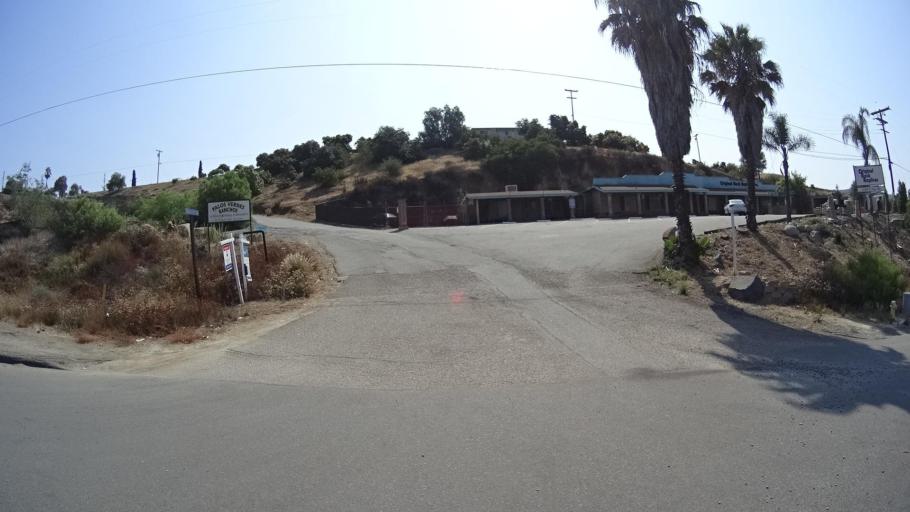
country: US
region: California
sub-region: San Diego County
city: Hidden Meadows
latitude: 33.2820
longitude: -117.1480
